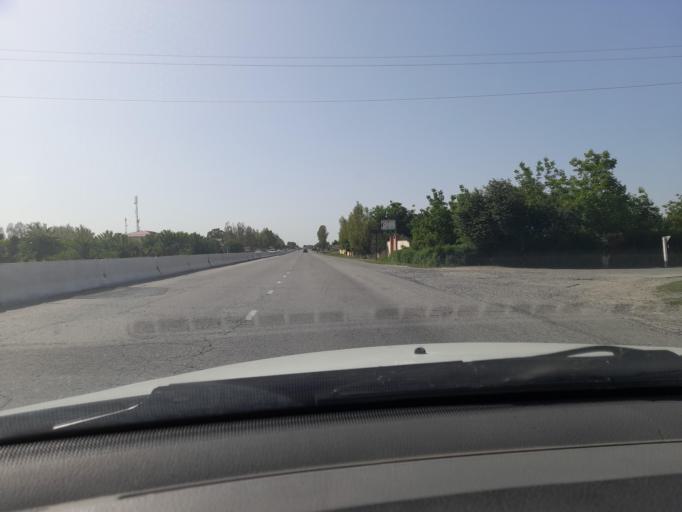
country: UZ
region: Samarqand
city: Chelak
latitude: 39.8378
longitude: 66.8238
